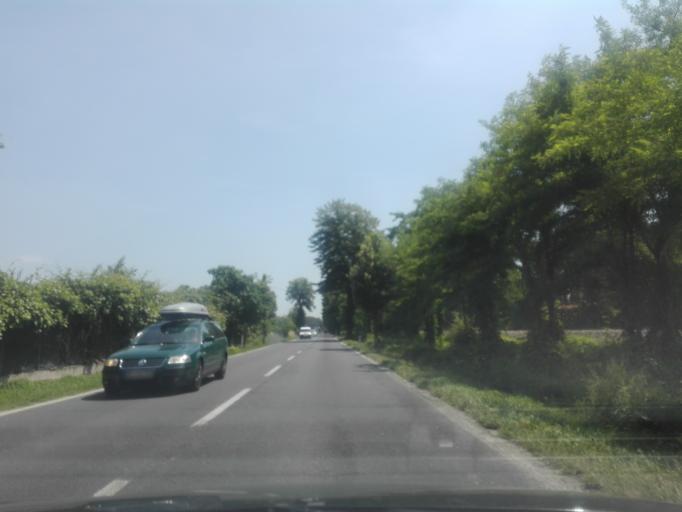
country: IT
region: Veneto
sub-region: Provincia di Rovigo
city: Adria
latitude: 45.0613
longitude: 12.0252
